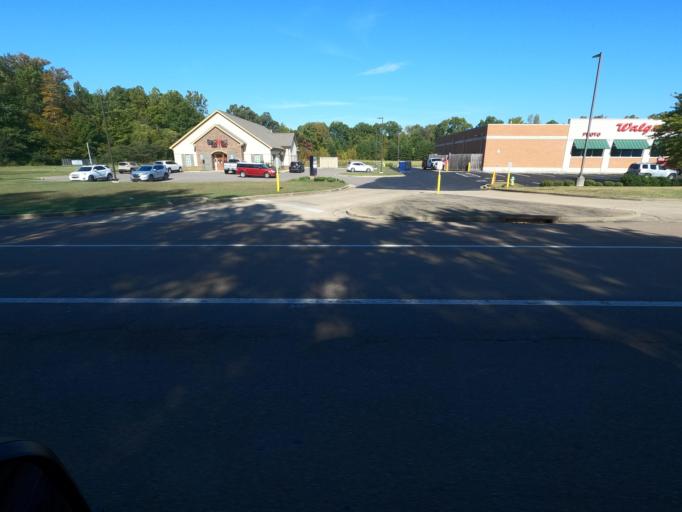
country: US
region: Tennessee
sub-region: Tipton County
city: Atoka
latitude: 35.4423
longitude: -89.7929
